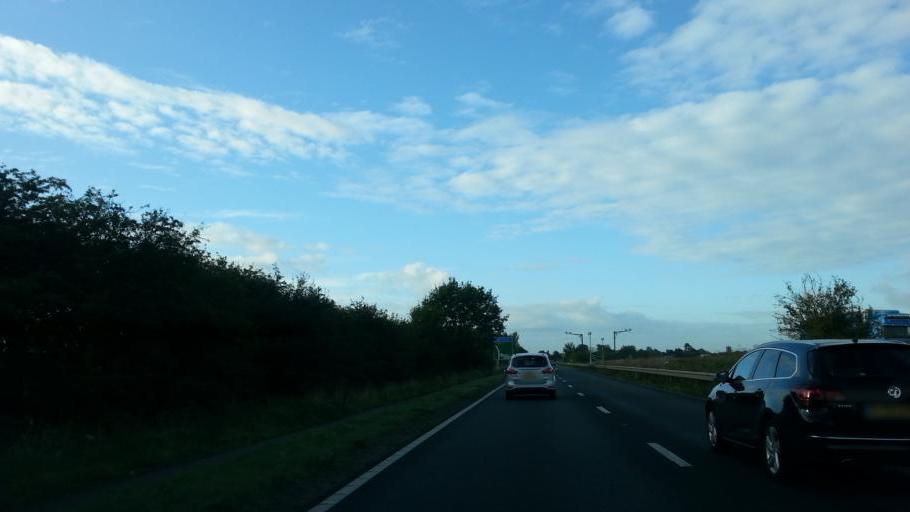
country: GB
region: England
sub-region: Cambridgeshire
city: Little Paxton
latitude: 52.2731
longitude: -0.2595
